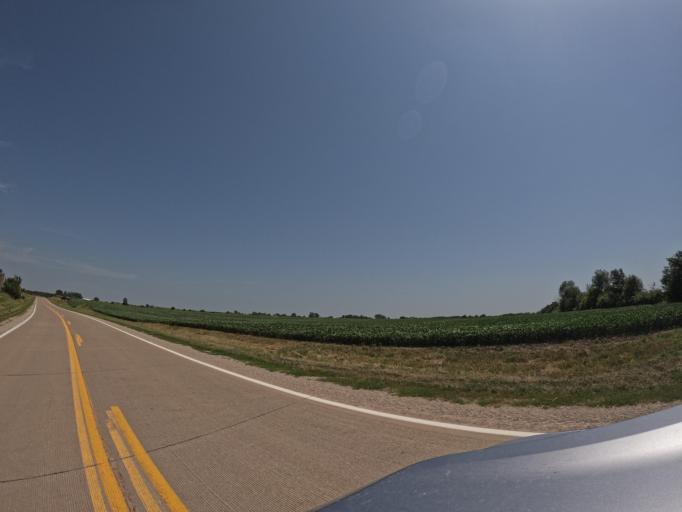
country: US
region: Iowa
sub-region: Henry County
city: Mount Pleasant
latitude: 40.9817
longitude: -91.6265
